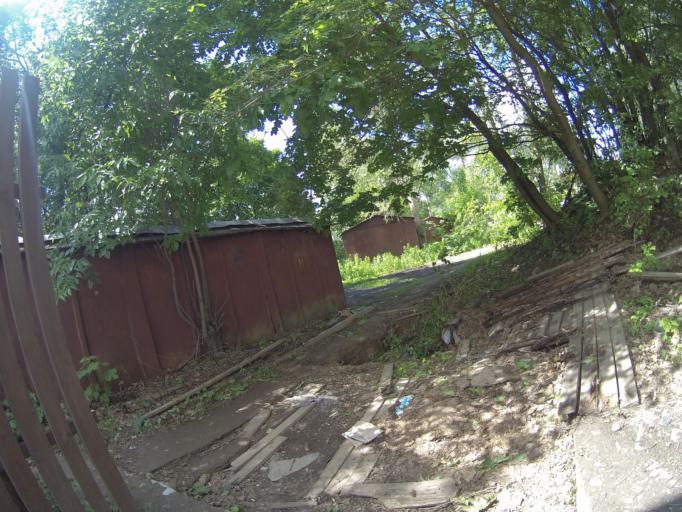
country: RU
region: Vladimir
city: Kommunar
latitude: 56.1560
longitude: 40.4531
